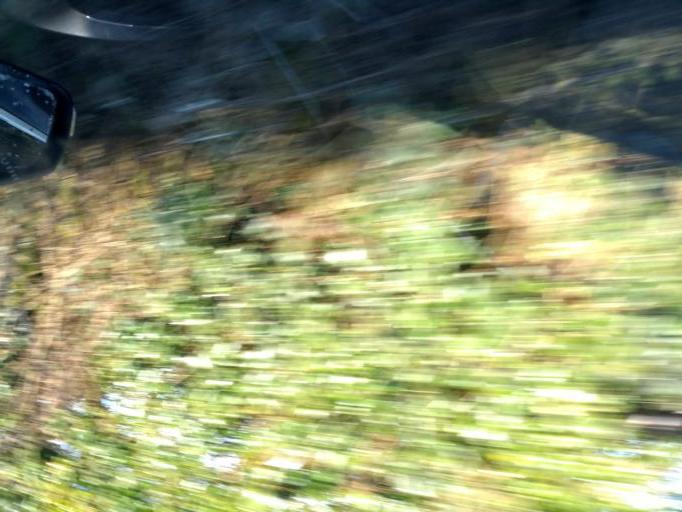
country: IE
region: Connaught
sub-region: County Galway
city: Athenry
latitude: 53.1887
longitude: -8.7881
